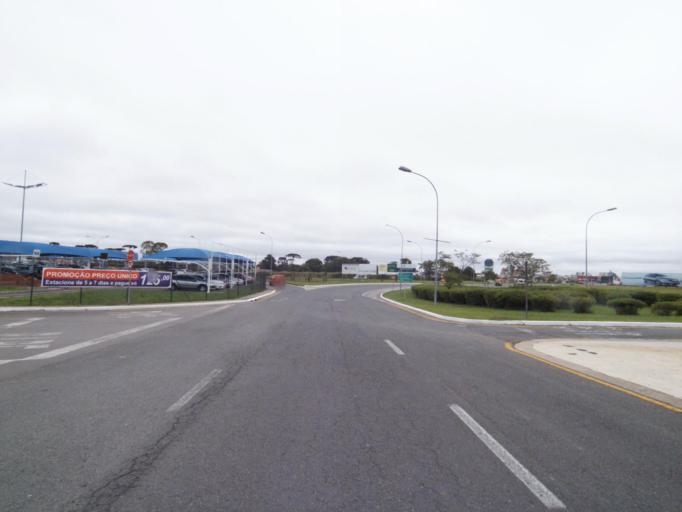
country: BR
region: Parana
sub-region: Sao Jose Dos Pinhais
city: Sao Jose dos Pinhais
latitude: -25.5356
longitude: -49.1765
